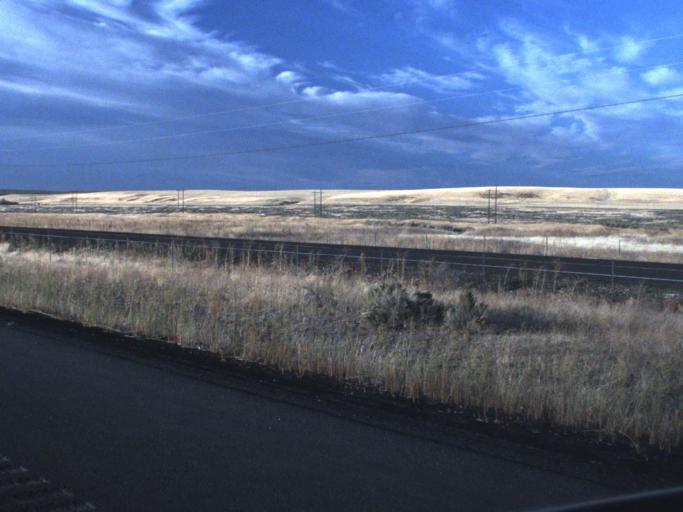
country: US
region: Washington
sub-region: Adams County
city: Ritzville
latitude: 47.1005
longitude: -118.4086
